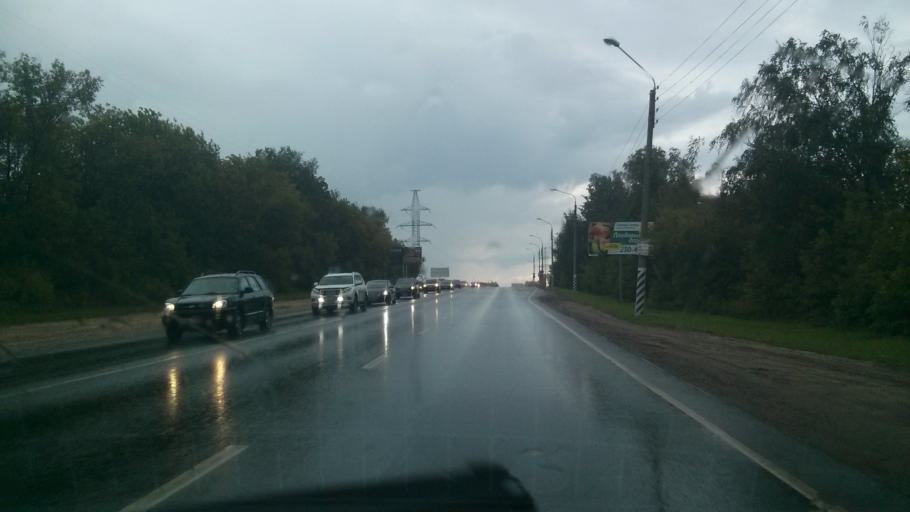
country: RU
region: Nizjnij Novgorod
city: Afonino
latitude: 56.2509
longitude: 44.0984
